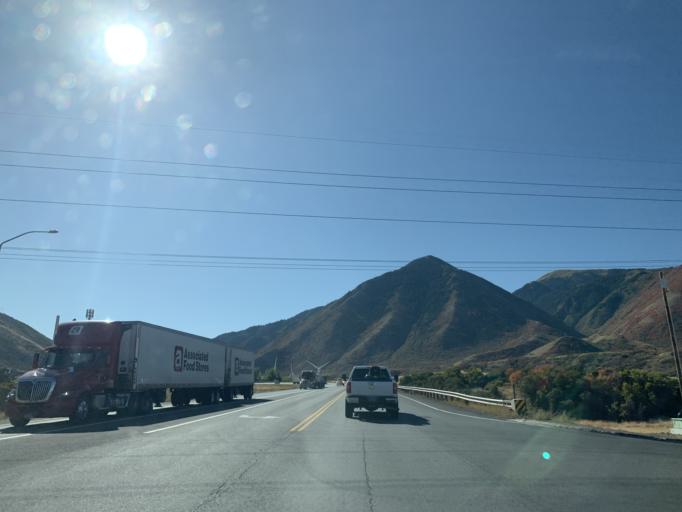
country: US
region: Utah
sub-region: Utah County
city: Mapleton
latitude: 40.0867
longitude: -111.5949
